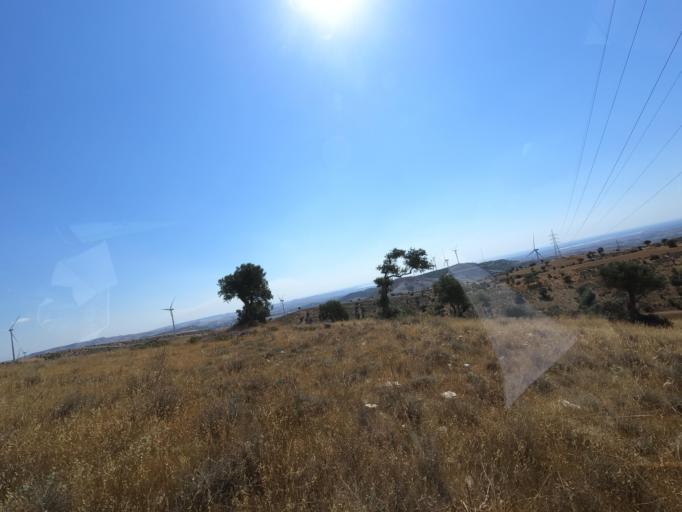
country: CY
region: Larnaka
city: Psevdas
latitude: 34.9581
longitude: 33.4835
